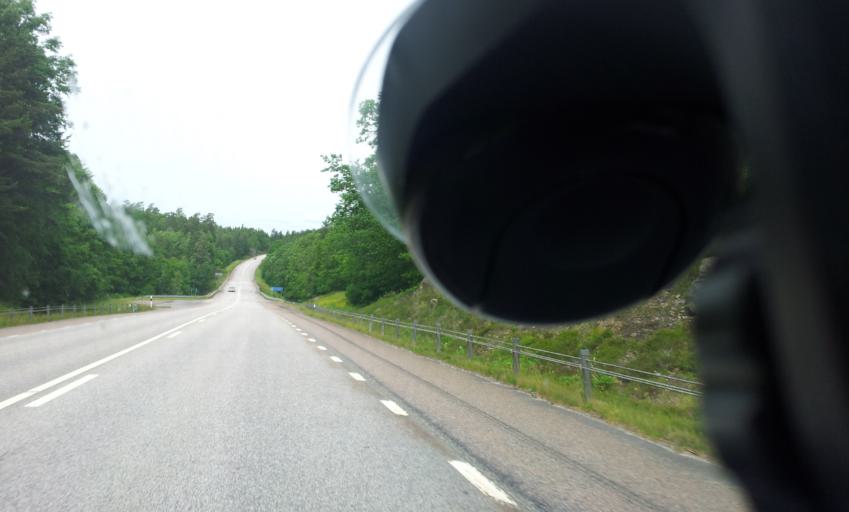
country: SE
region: Kalmar
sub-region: Vasterviks Kommun
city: Ankarsrum
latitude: 57.5477
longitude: 16.4779
